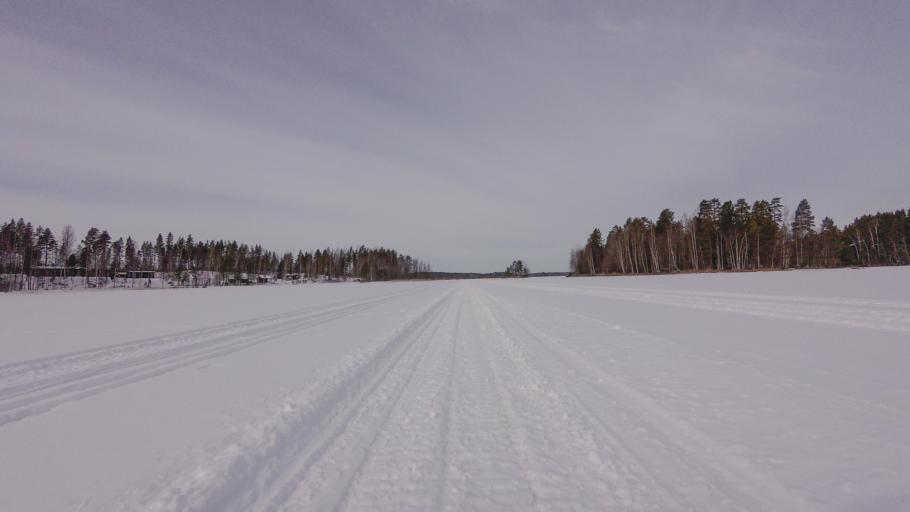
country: FI
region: Southern Savonia
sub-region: Savonlinna
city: Heinaevesi
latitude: 62.1236
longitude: 28.6116
